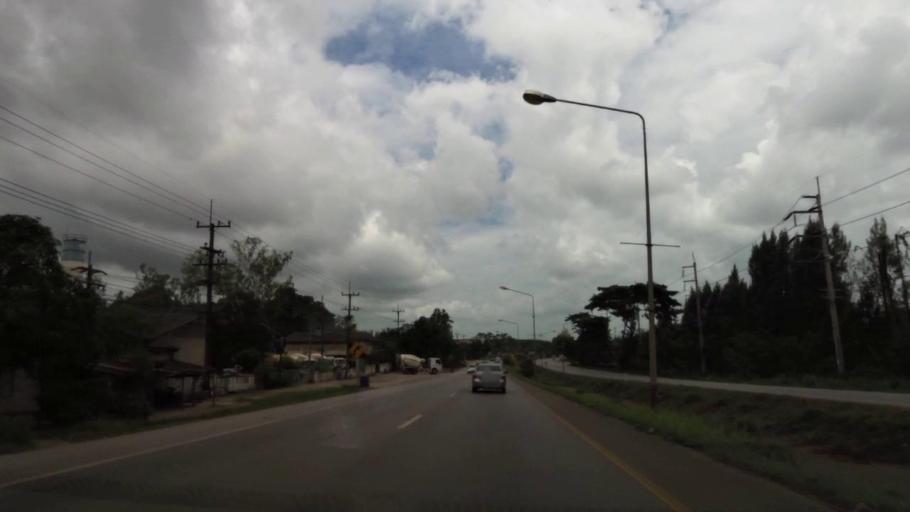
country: TH
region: Chanthaburi
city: Na Yai Am
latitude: 12.7830
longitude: 101.7997
